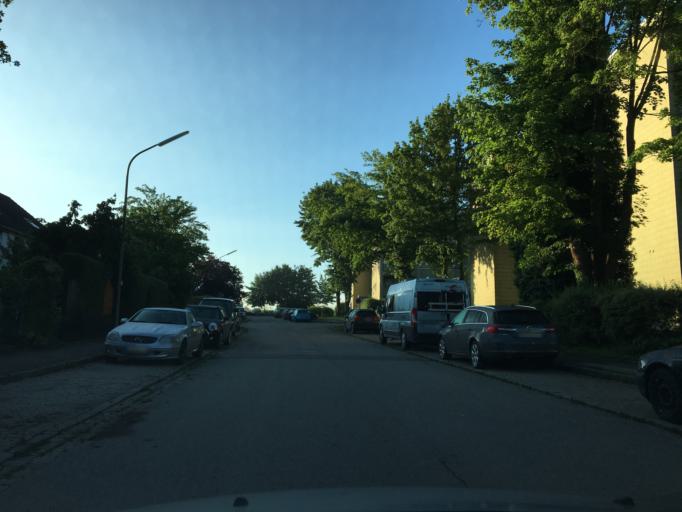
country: DE
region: Bavaria
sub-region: Upper Bavaria
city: Haimhausen
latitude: 48.3128
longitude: 11.5522
